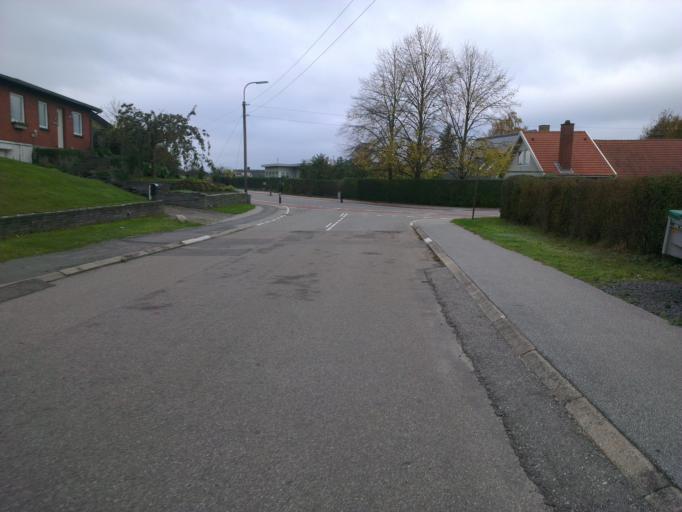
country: DK
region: Capital Region
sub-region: Frederikssund Kommune
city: Jaegerspris
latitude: 55.8529
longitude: 11.9955
